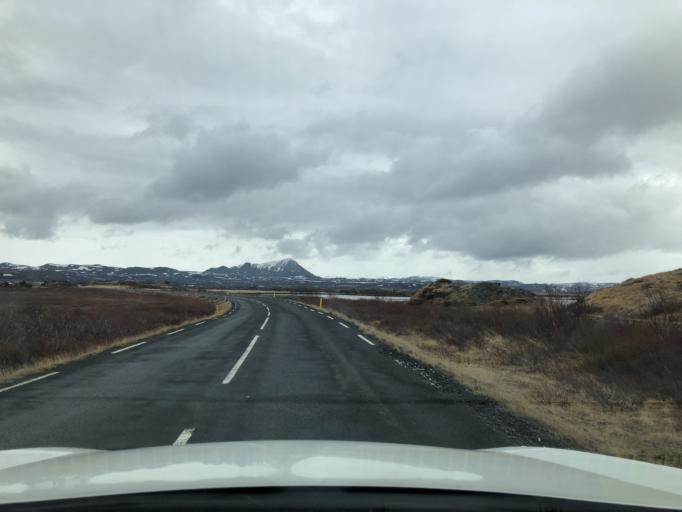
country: IS
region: Northeast
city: Laugar
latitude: 65.6296
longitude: -17.0159
